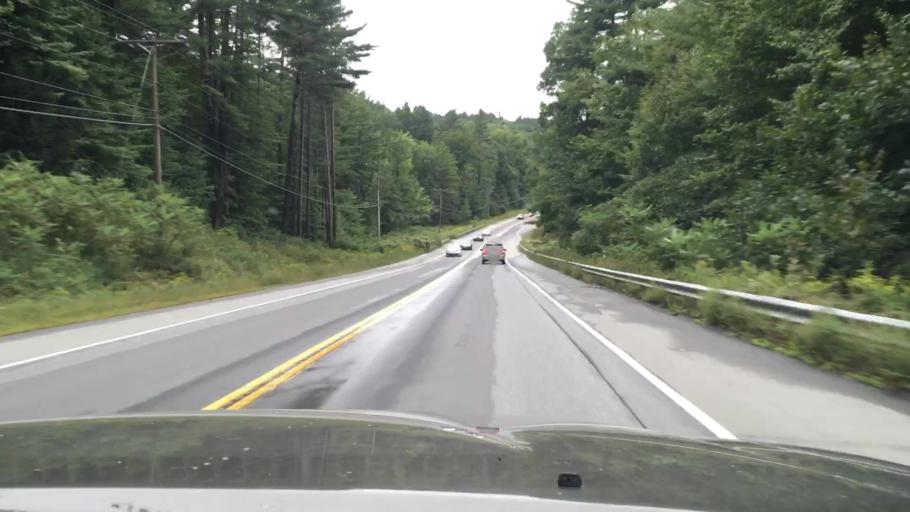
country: US
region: Vermont
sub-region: Windham County
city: Brattleboro
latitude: 42.8920
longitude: -72.5268
